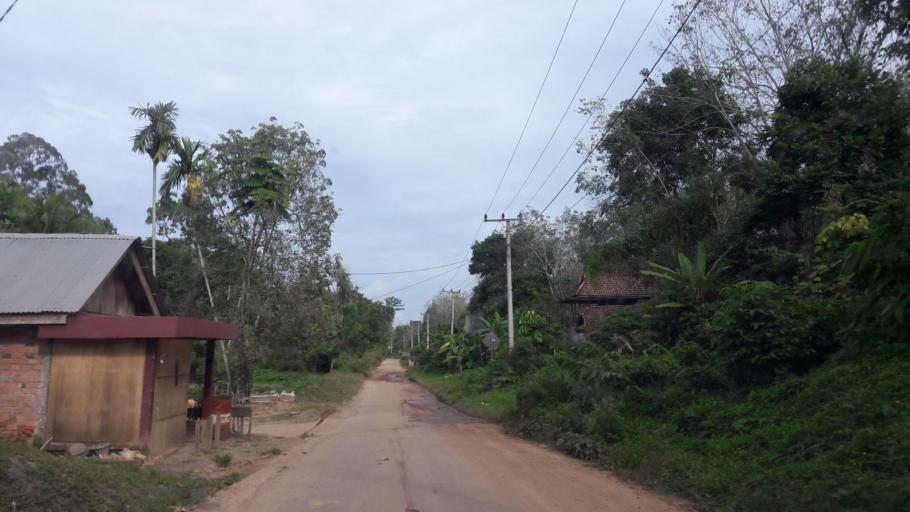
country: ID
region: South Sumatra
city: Gunungmegang Dalam
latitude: -3.2862
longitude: 103.7255
